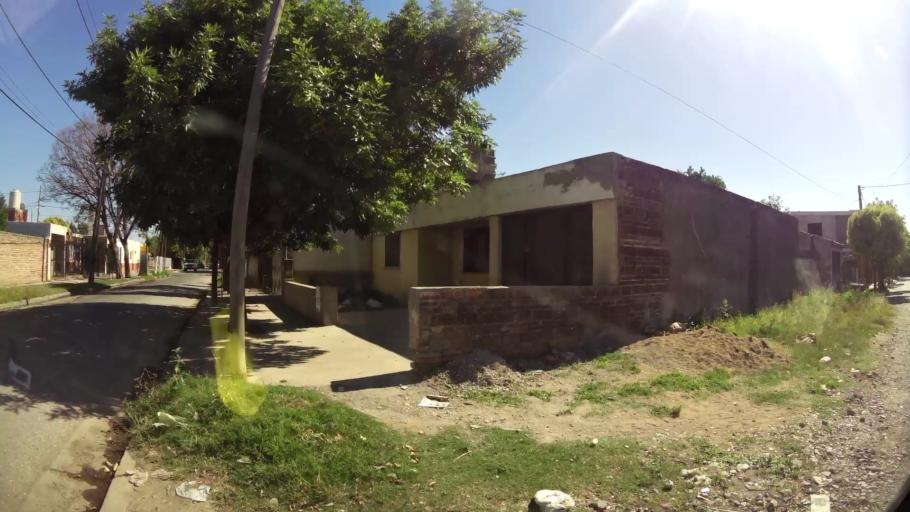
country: AR
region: Cordoba
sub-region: Departamento de Capital
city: Cordoba
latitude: -31.4431
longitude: -64.1390
